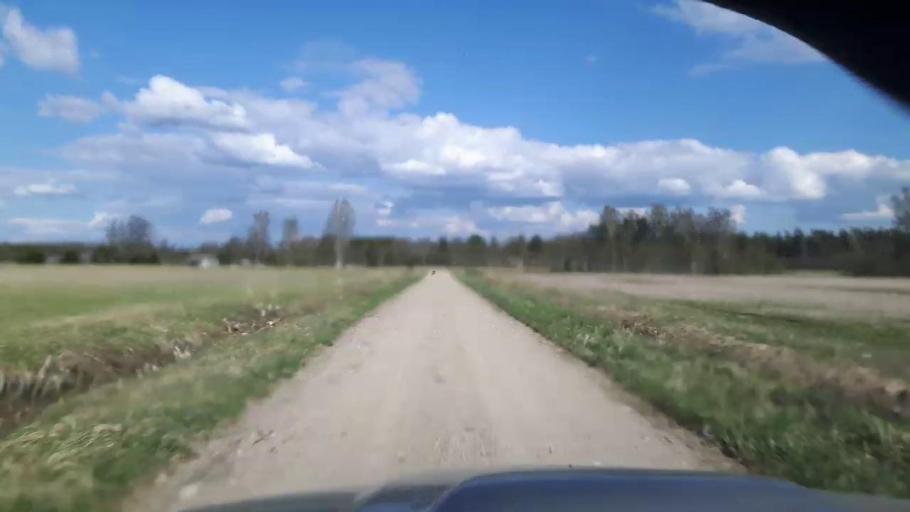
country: EE
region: Paernumaa
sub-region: Tootsi vald
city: Tootsi
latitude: 58.4360
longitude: 24.8704
